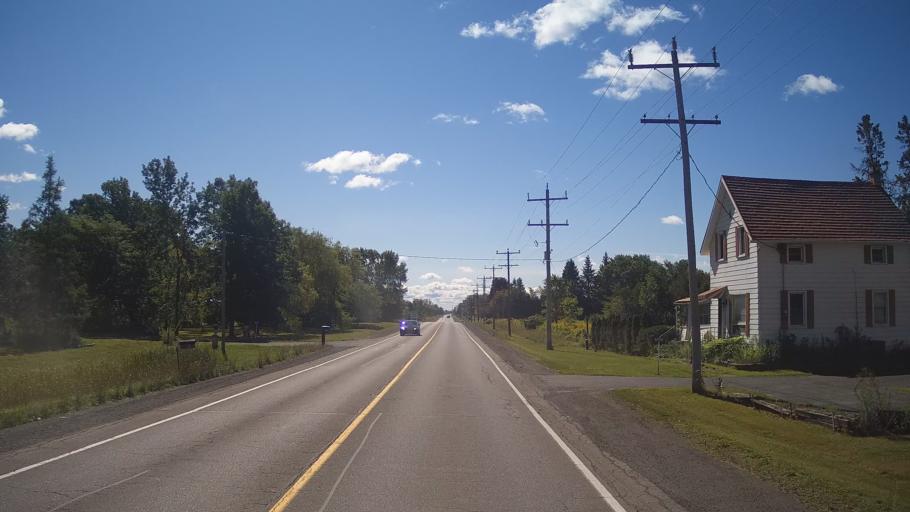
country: US
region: New York
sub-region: St. Lawrence County
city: Norfolk
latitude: 44.9339
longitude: -75.2115
